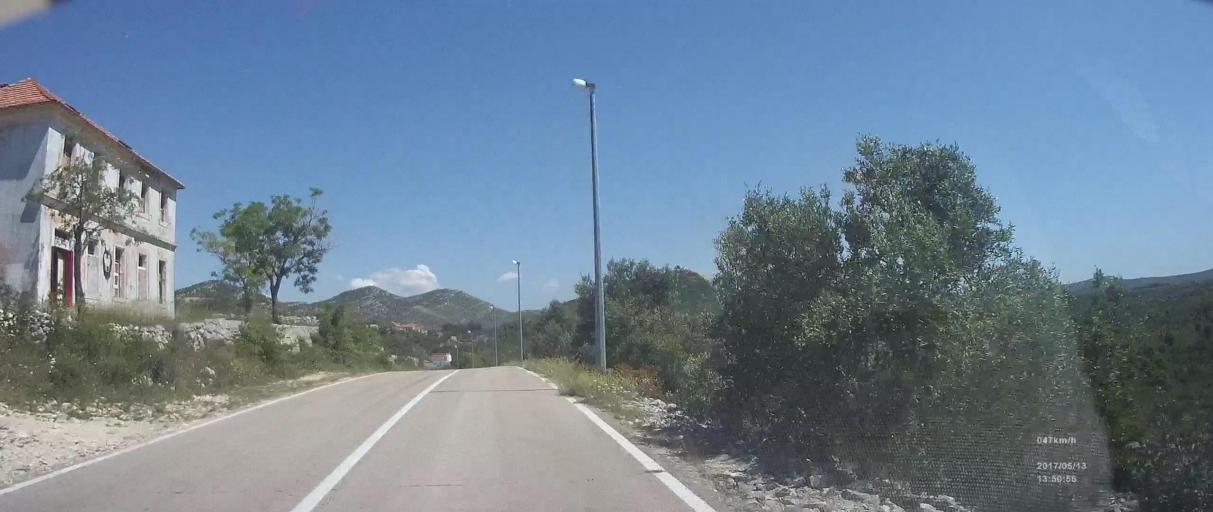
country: HR
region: Sibensko-Kniniska
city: Primosten
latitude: 43.6092
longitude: 15.9865
